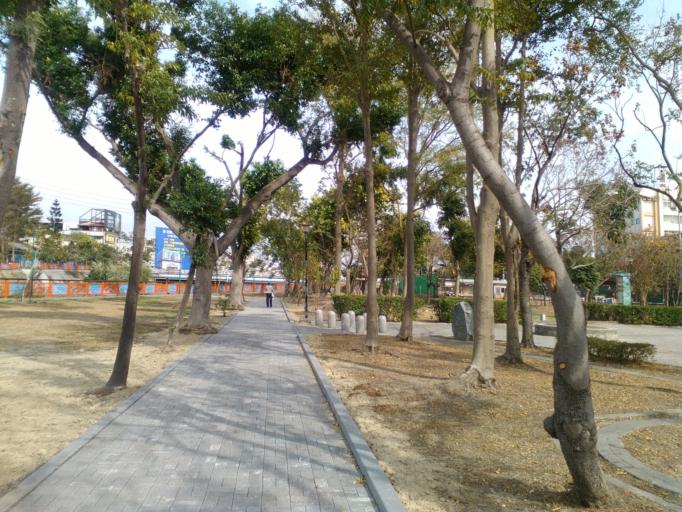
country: TW
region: Taiwan
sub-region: Taichung City
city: Taichung
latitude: 24.1171
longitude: 120.6774
